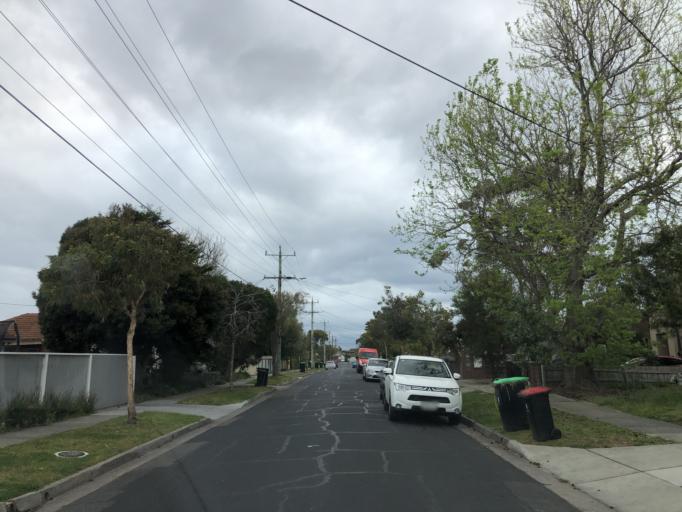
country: AU
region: Victoria
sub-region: Kingston
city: Bonbeach
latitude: -38.0587
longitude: 145.1280
